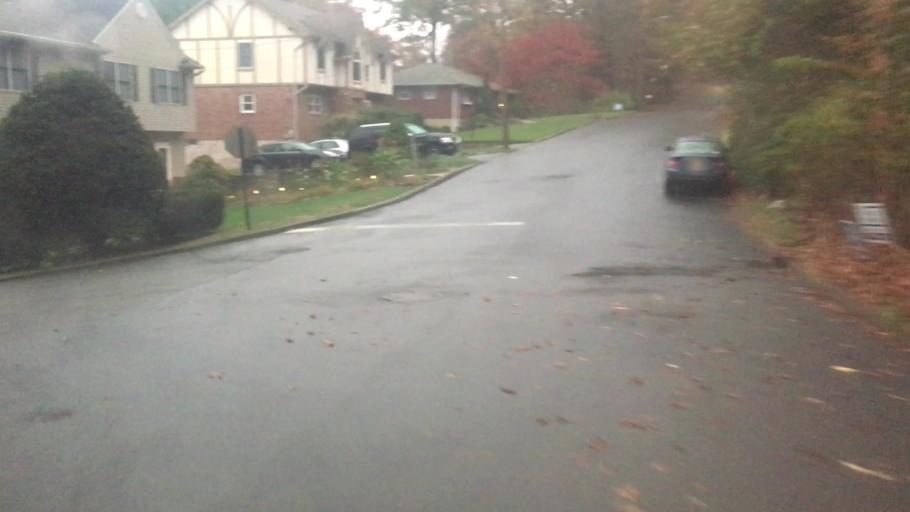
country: US
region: New Jersey
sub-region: Passaic County
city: Bloomingdale
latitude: 41.0139
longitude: -74.3285
